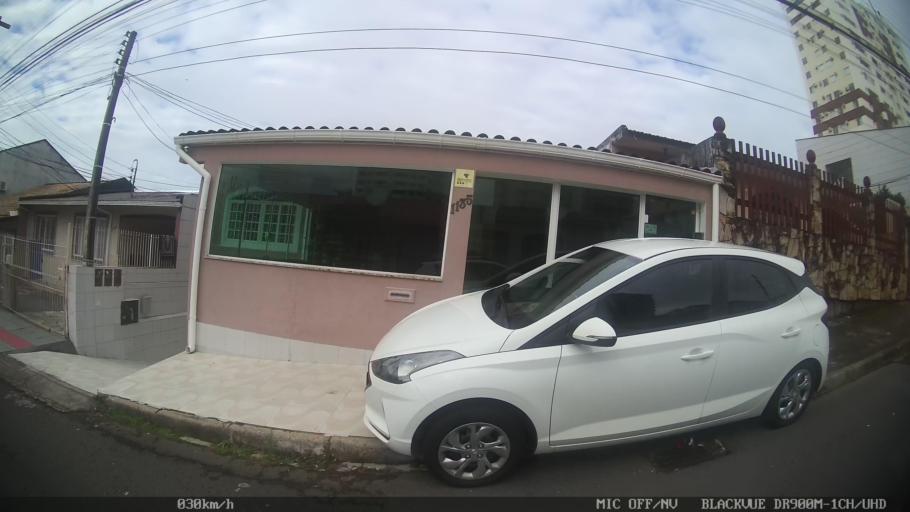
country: BR
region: Santa Catarina
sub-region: Sao Jose
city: Campinas
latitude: -27.5832
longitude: -48.6063
